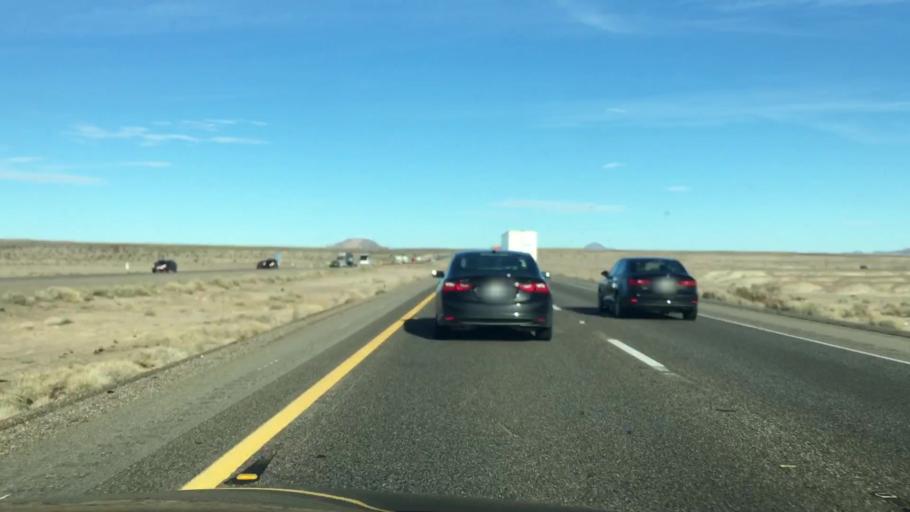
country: US
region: California
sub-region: San Bernardino County
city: Fort Irwin
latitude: 34.9955
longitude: -116.5712
